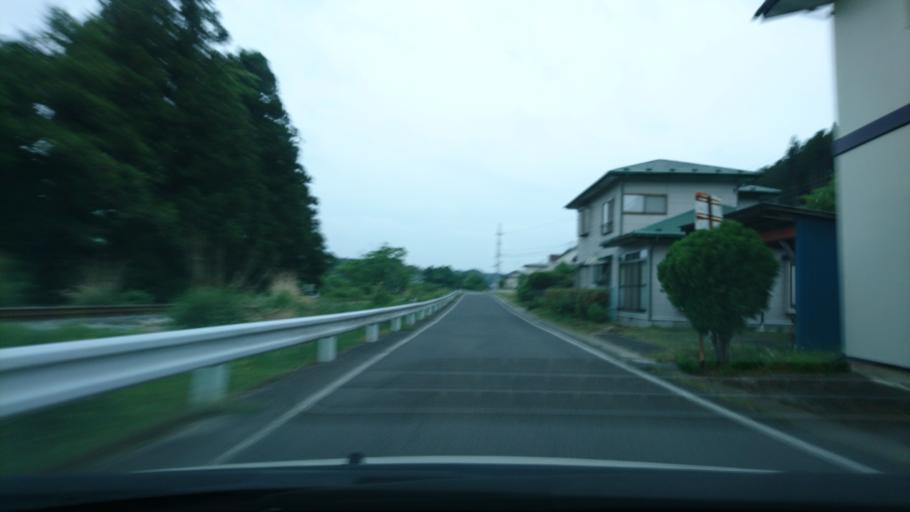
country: JP
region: Iwate
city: Ichinoseki
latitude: 38.9147
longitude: 141.1758
